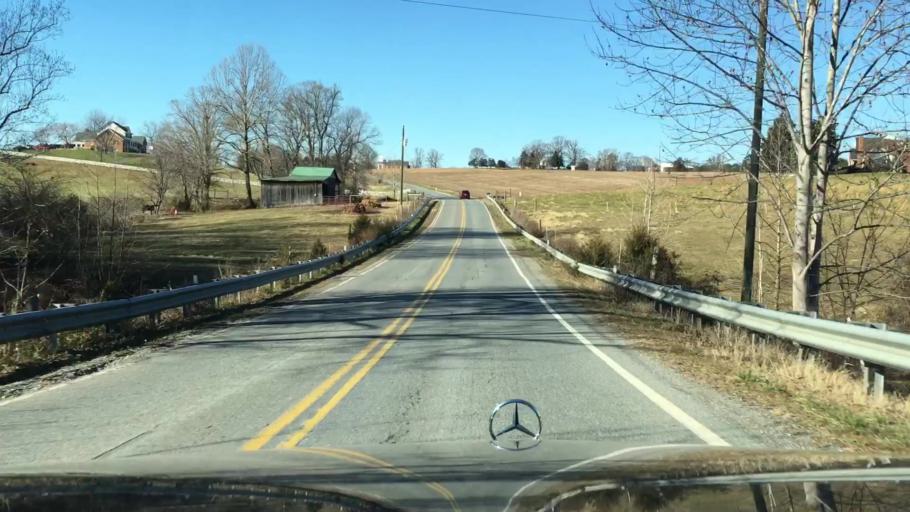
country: US
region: Virginia
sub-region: Pittsylvania County
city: Motley
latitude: 37.1878
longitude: -79.4205
